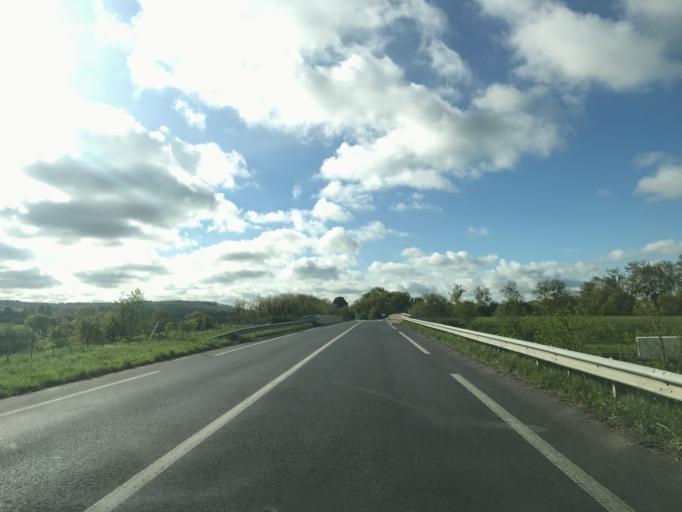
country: FR
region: Lower Normandy
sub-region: Departement du Calvados
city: Dozule
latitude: 49.2289
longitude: -0.0847
